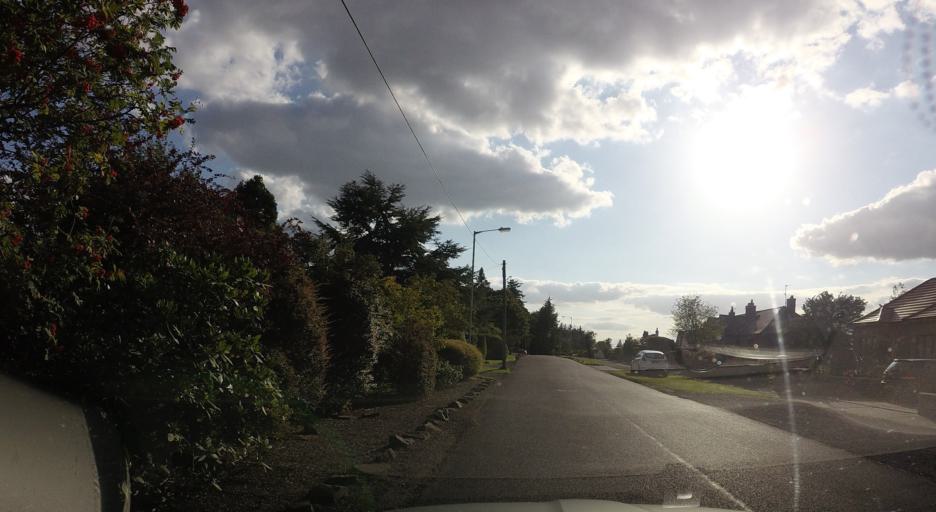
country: GB
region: Scotland
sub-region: Angus
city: Muirhead
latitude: 56.4554
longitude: -3.0640
